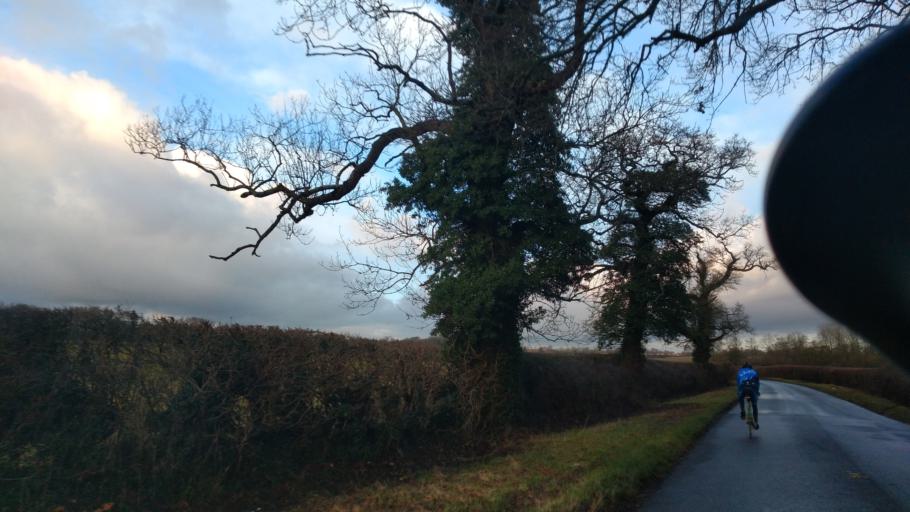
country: GB
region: England
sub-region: Wiltshire
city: Corsham
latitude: 51.4458
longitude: -2.1859
